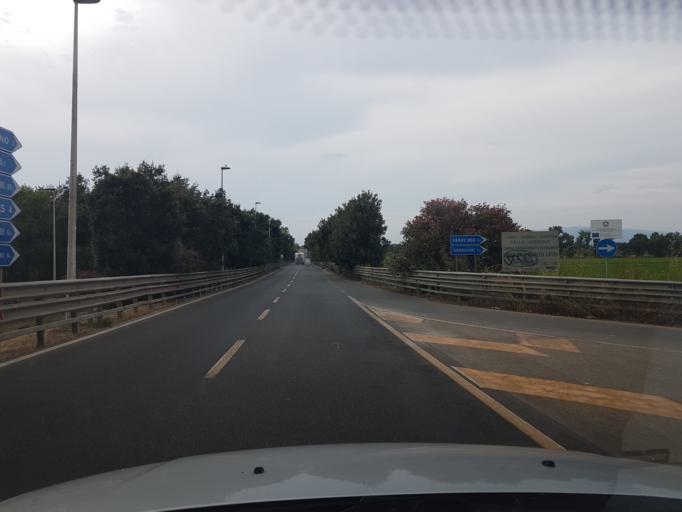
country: IT
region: Sardinia
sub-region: Provincia di Oristano
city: Donigala Fenugheddu
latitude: 39.9225
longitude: 8.5814
